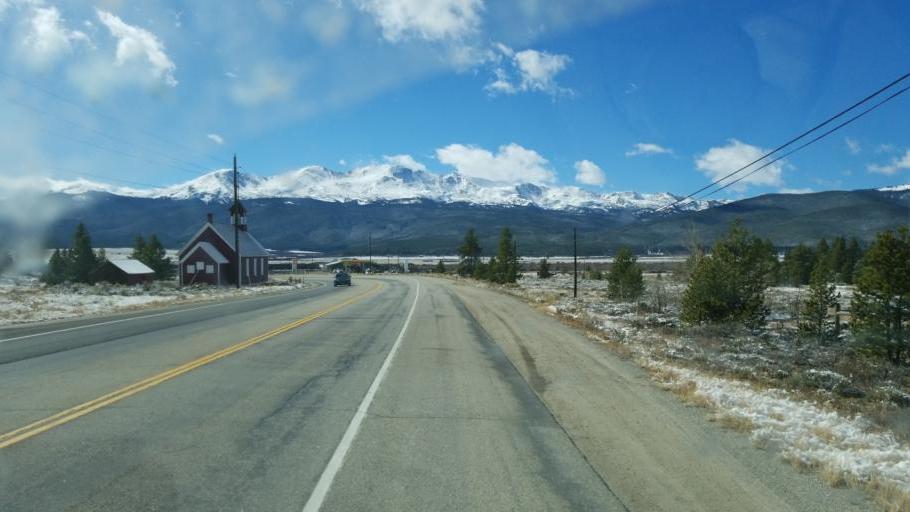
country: US
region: Colorado
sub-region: Lake County
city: Leadville North
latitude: 39.2247
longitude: -106.3453
